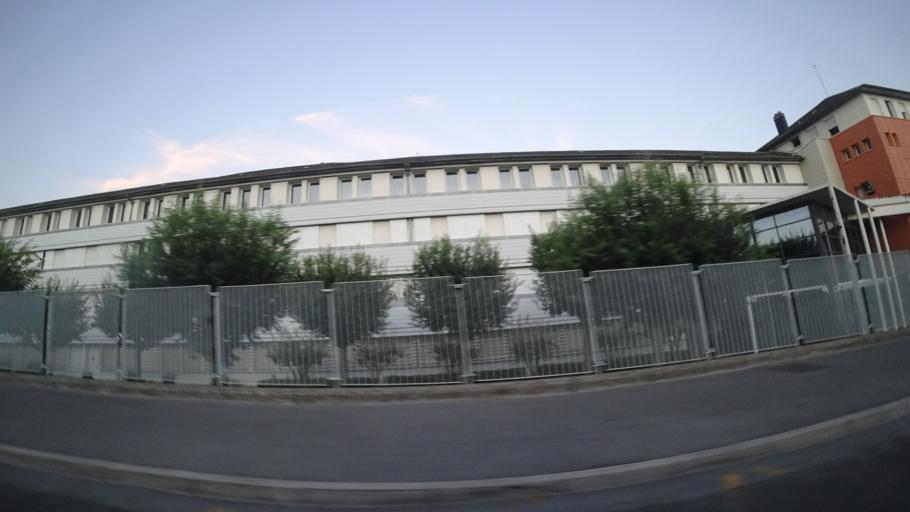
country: FR
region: Midi-Pyrenees
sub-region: Departement de l'Aveyron
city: Millau
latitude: 44.0975
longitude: 3.0730
